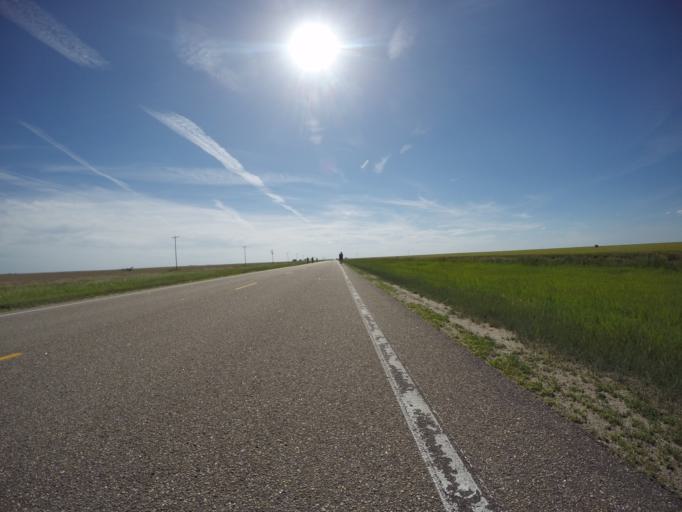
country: US
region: Kansas
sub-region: Cheyenne County
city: Saint Francis
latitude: 39.7567
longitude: -101.9689
